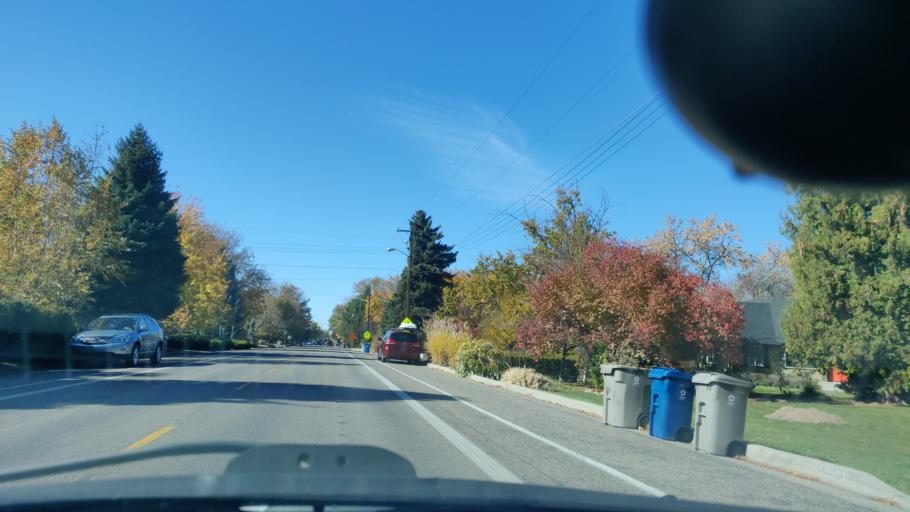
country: US
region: Idaho
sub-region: Ada County
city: Boise
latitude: 43.5935
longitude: -116.2254
